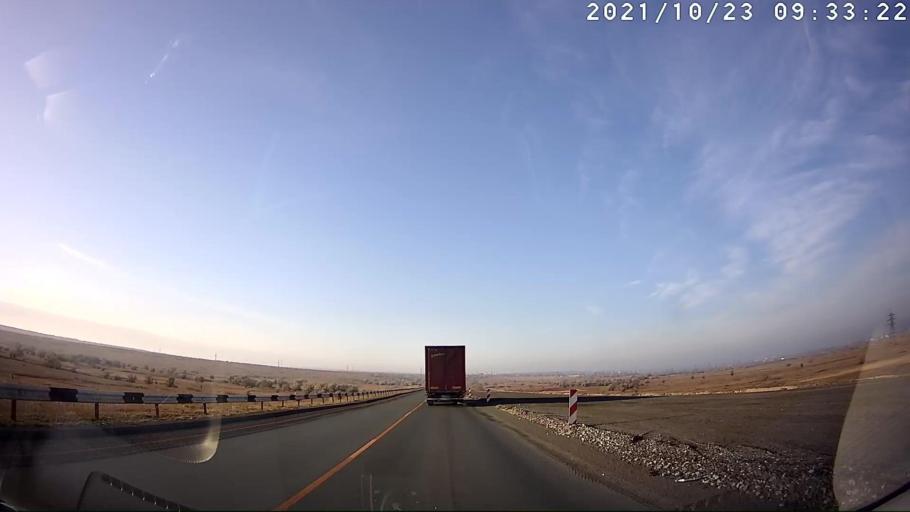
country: RU
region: Saratov
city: Sokolovyy
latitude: 51.6625
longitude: 45.8504
